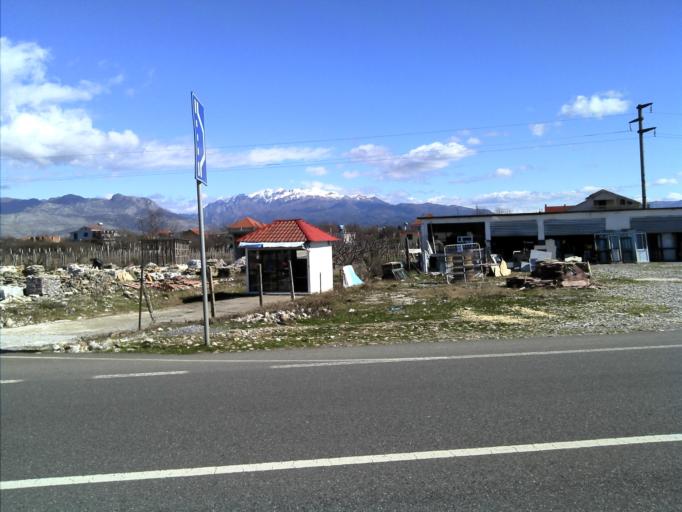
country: AL
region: Shkoder
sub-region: Rrethi i Shkodres
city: Shkoder
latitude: 42.1010
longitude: 19.5048
